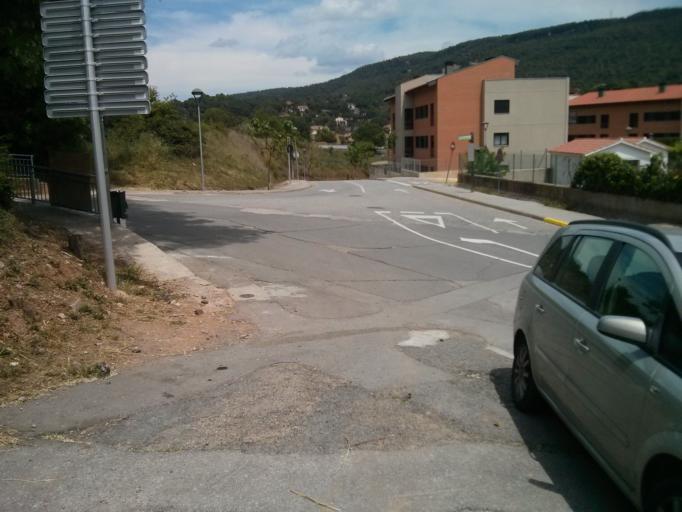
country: ES
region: Catalonia
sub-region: Provincia de Barcelona
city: Aiguafreda
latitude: 41.7637
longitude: 2.2497
